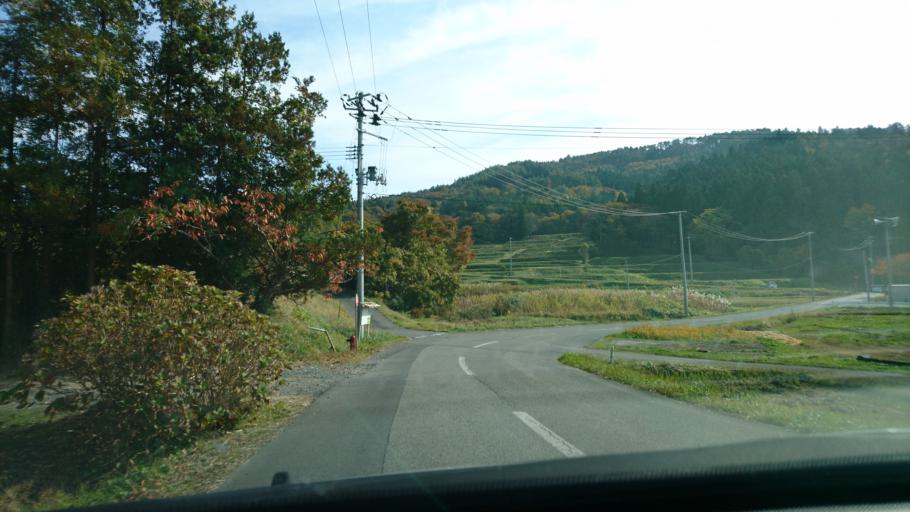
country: JP
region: Iwate
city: Ichinoseki
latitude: 38.9758
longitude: 141.1808
